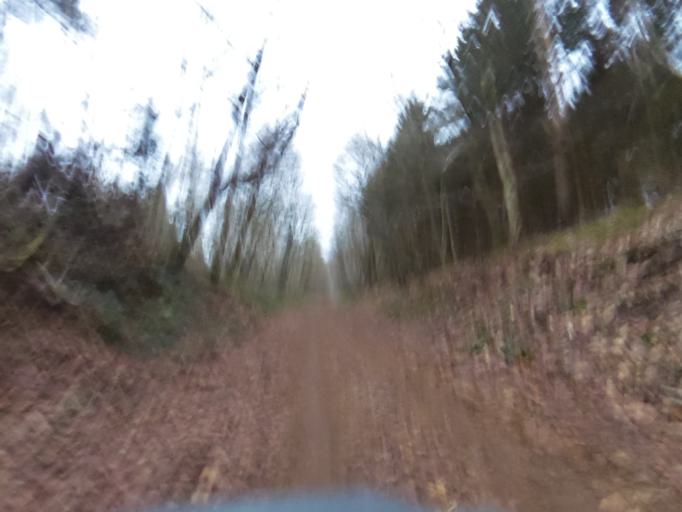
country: GB
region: England
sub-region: Norfolk
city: Costessey
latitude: 52.7083
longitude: 1.1747
